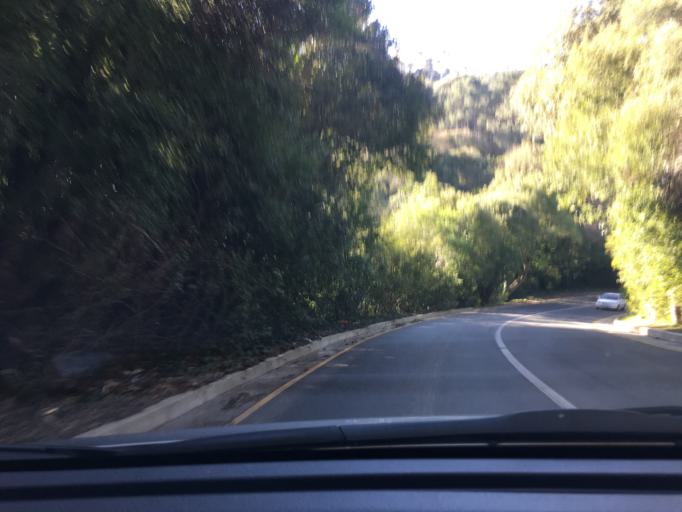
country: ZA
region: Western Cape
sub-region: City of Cape Town
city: Constantia
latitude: -34.0105
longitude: 18.4086
